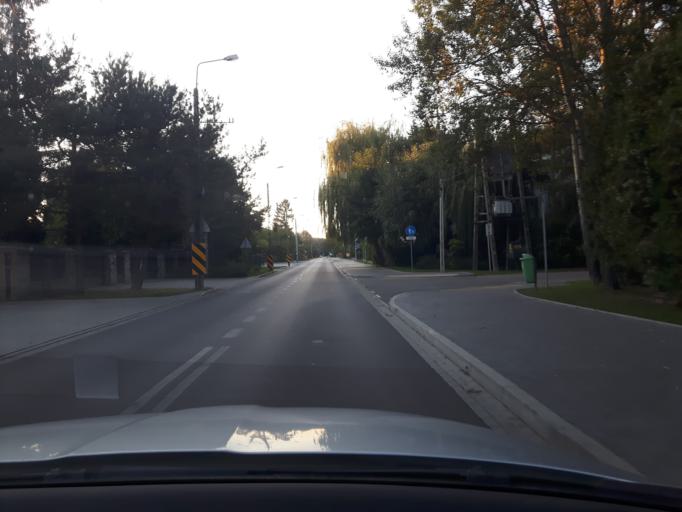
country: PL
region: Masovian Voivodeship
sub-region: Powiat wolominski
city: Kobylka
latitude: 52.3318
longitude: 21.1915
